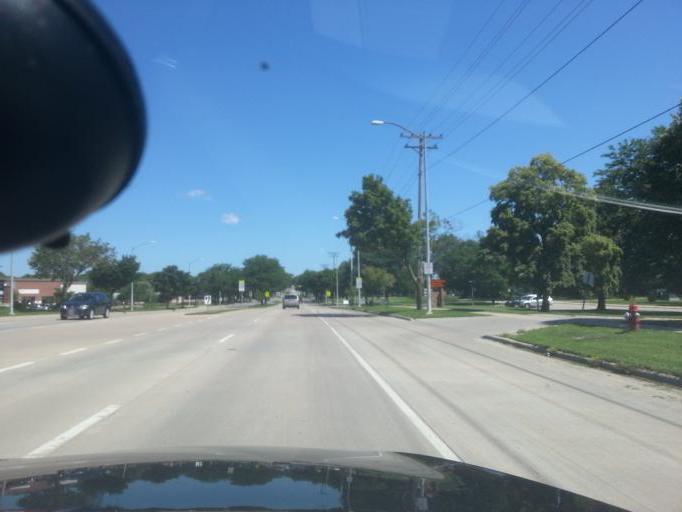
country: US
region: Wisconsin
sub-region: Dane County
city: Middleton
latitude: 43.0628
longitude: -89.5026
